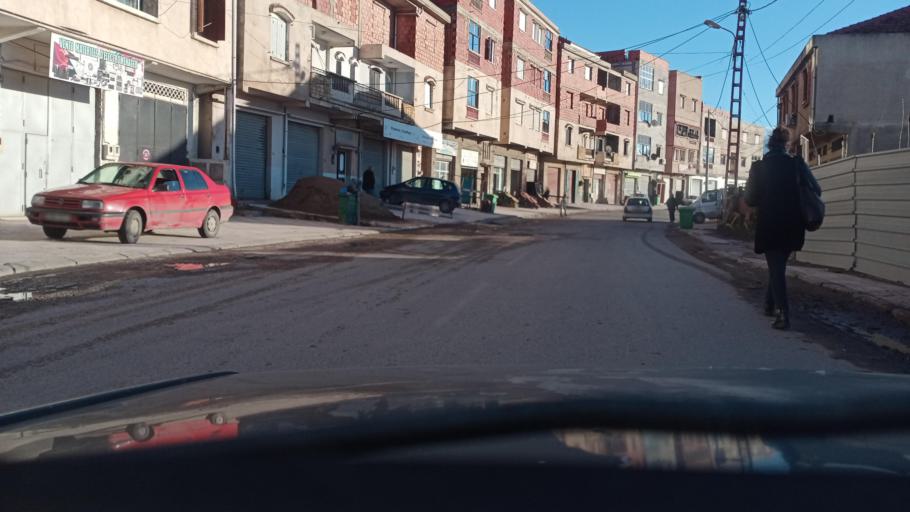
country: DZ
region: Tizi Ouzou
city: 'Ain el Hammam
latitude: 36.5624
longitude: 4.3240
